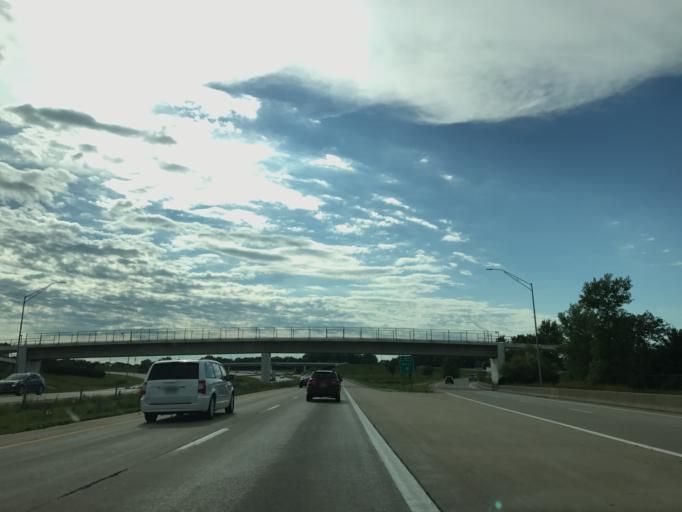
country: US
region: Iowa
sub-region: Polk County
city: Clive
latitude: 41.5922
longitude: -93.8031
